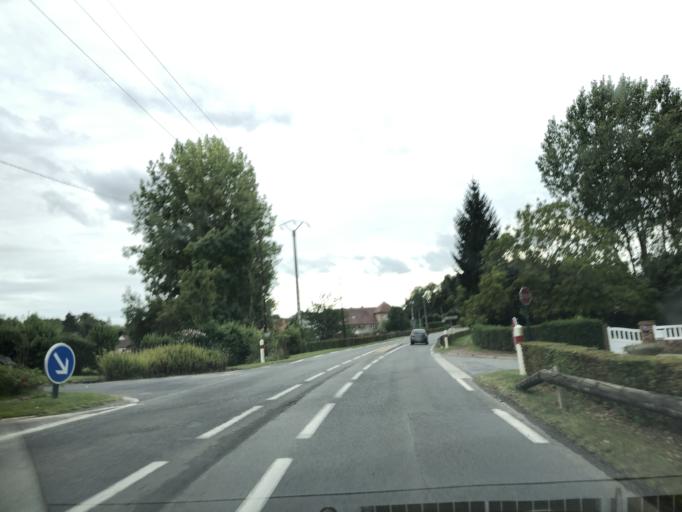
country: FR
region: Picardie
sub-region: Departement de la Somme
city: Chepy
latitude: 50.0956
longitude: 1.7204
